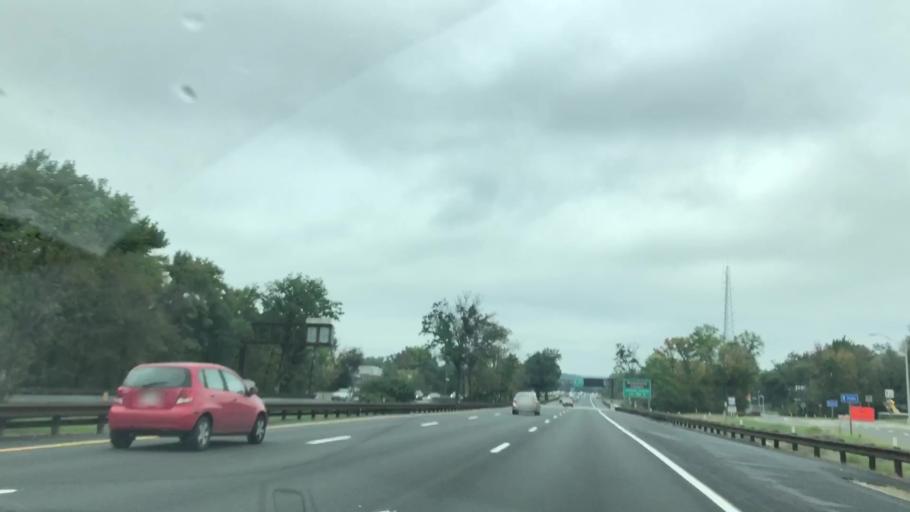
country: US
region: New Jersey
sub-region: Essex County
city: Brookdale
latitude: 40.8368
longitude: -74.1794
